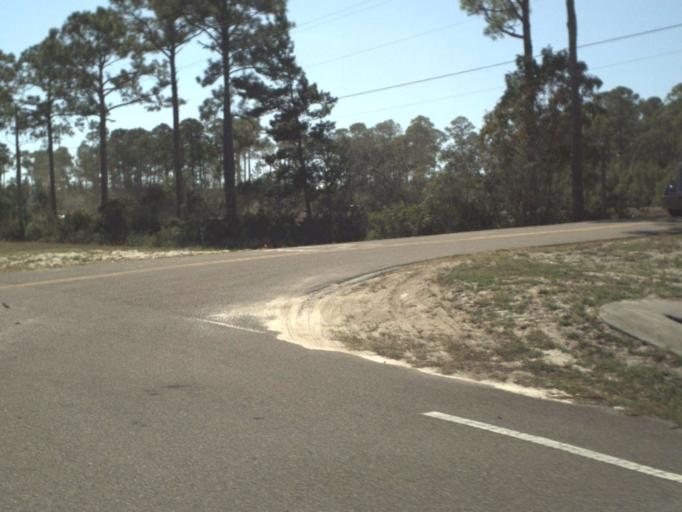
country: US
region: Florida
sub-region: Bay County
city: Laguna Beach
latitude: 30.2876
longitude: -86.0173
